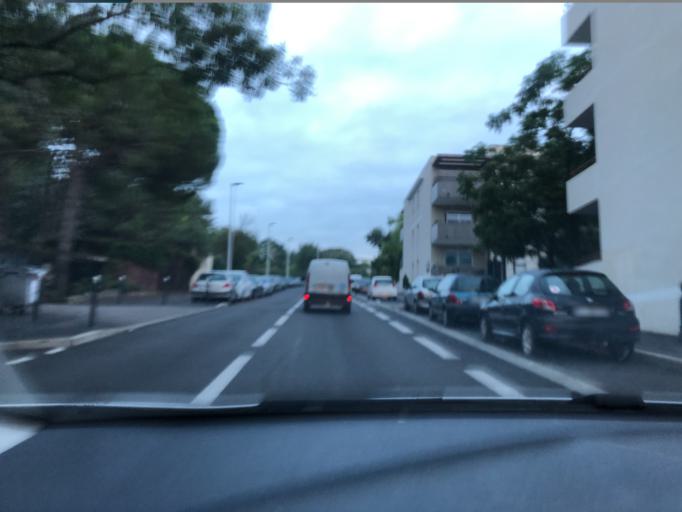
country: FR
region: Languedoc-Roussillon
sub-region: Departement de l'Herault
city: Montferrier-sur-Lez
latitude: 43.6389
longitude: 3.8390
